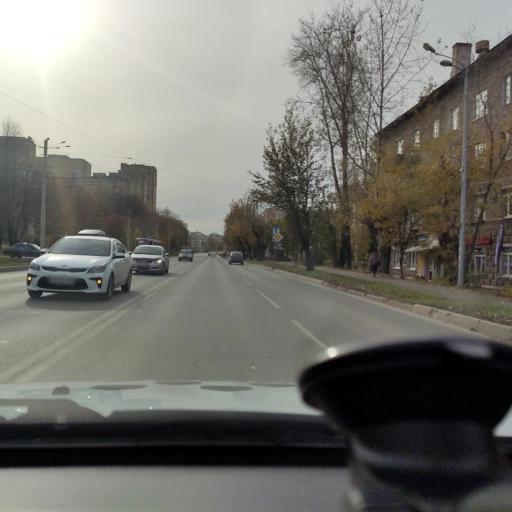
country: RU
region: Perm
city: Perm
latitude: 58.0251
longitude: 56.2894
